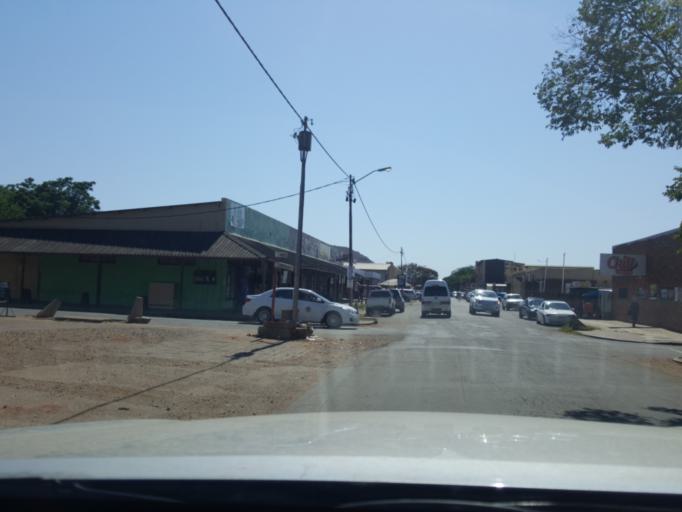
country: ZA
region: North-West
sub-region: Ngaka Modiri Molema District Municipality
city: Zeerust
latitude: -25.5447
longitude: 26.0765
